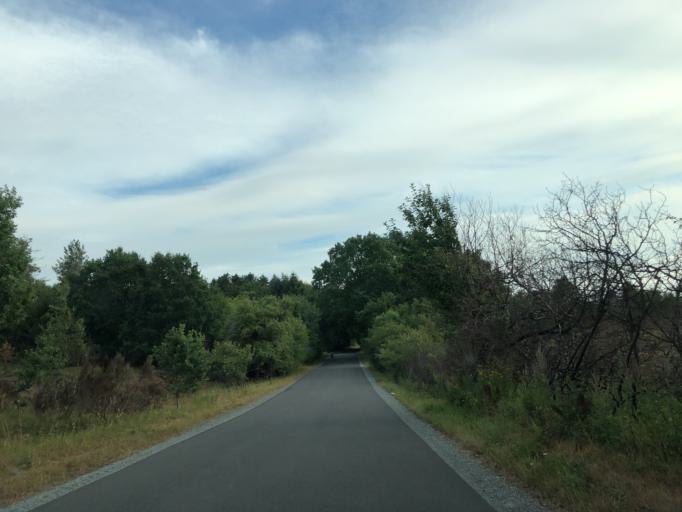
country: DK
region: South Denmark
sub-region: Vejle Kommune
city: Egtved
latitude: 55.6656
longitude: 9.2597
